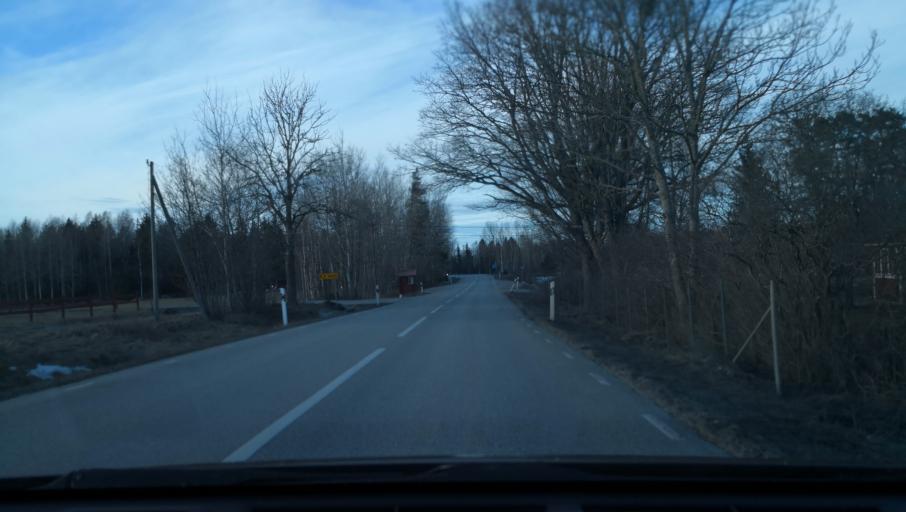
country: SE
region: Uppsala
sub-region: Osthammars Kommun
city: OEsthammar
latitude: 60.3076
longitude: 18.2706
